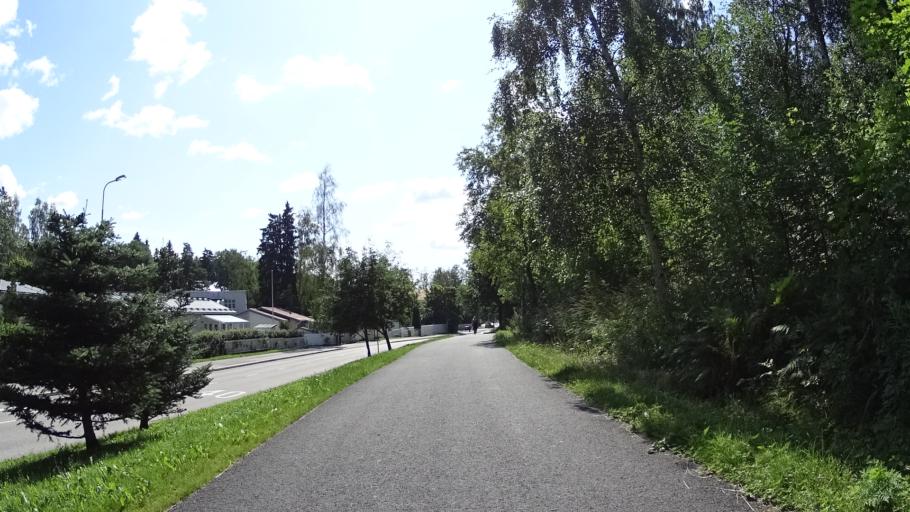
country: FI
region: Uusimaa
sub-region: Helsinki
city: Jaervenpaeae
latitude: 60.4784
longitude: 25.0730
